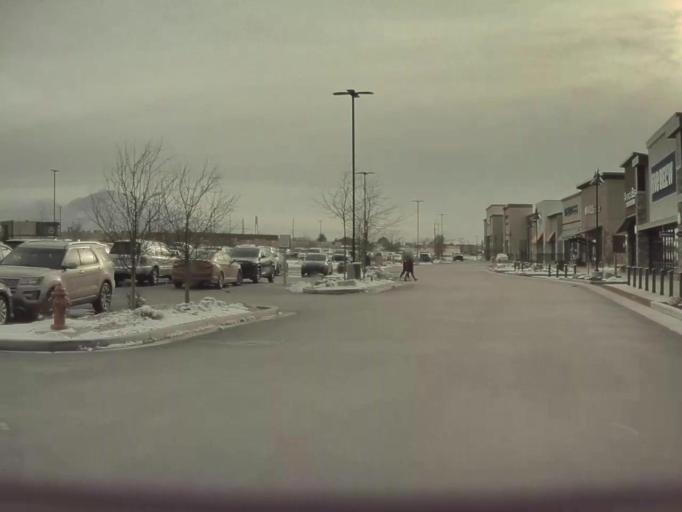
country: US
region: Utah
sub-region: Utah County
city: Spanish Fork
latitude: 40.1277
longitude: -111.6407
